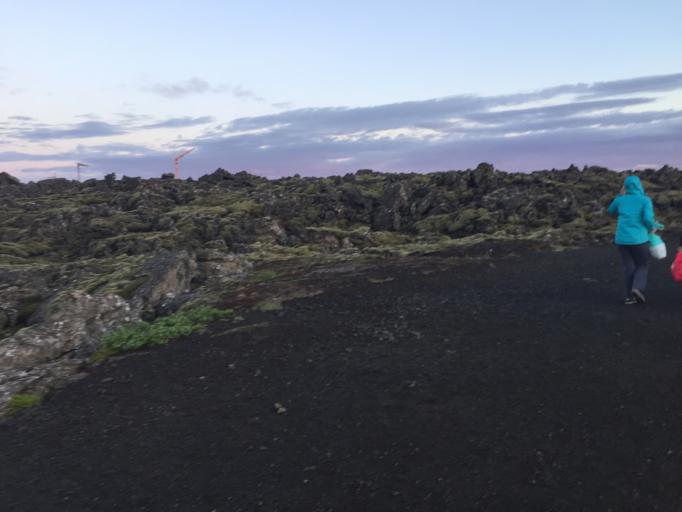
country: IS
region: Southern Peninsula
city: Grindavik
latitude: 63.8824
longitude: -22.4499
